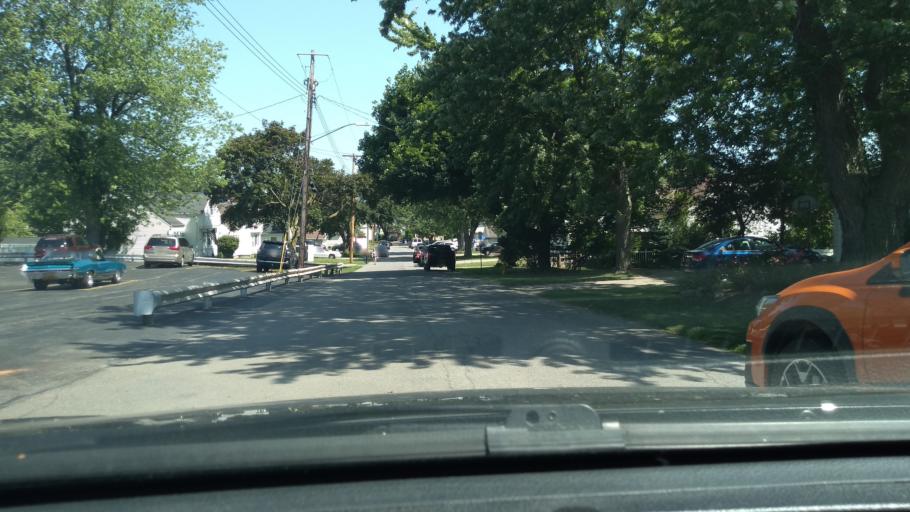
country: US
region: New York
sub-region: Erie County
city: West Seneca
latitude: 42.8347
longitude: -78.7504
